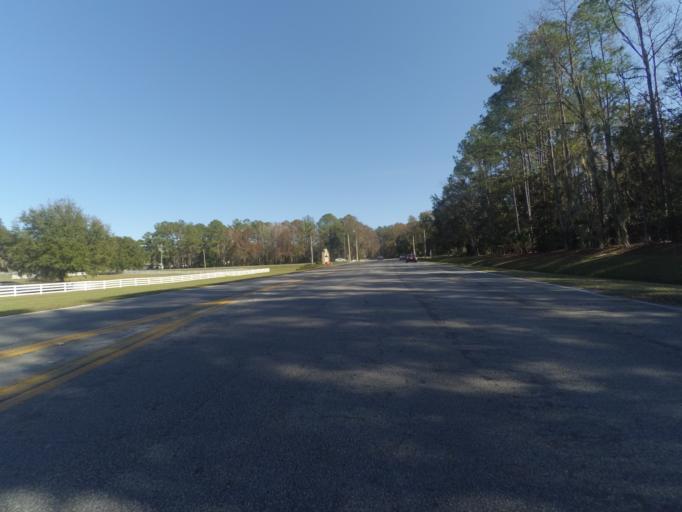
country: US
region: Florida
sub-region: Alachua County
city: Gainesville
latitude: 29.6103
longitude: -82.4239
